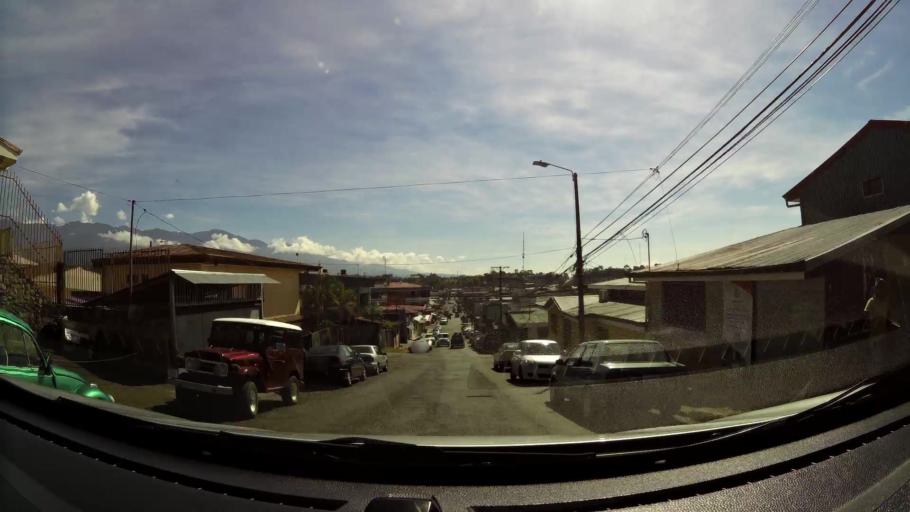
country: CR
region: San Jose
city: San Isidro
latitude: 9.3739
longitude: -83.7066
